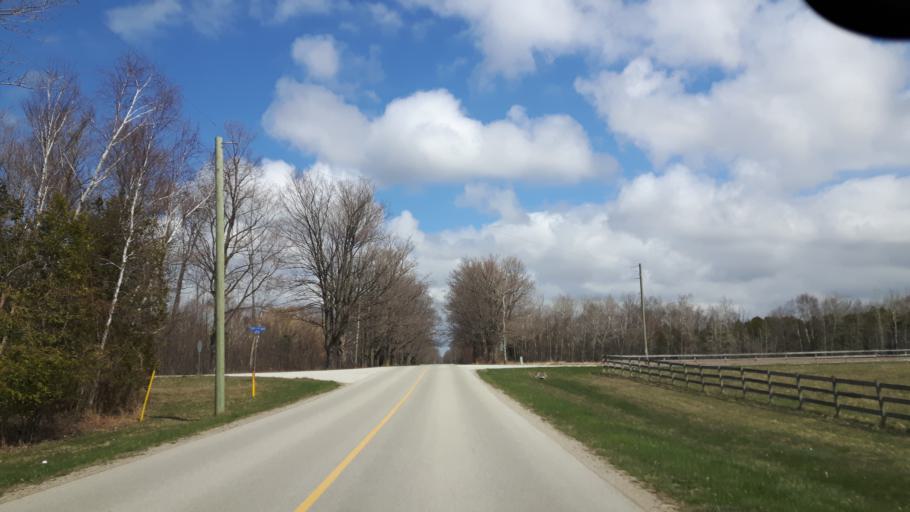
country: CA
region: Ontario
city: Goderich
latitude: 43.6236
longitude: -81.6846
